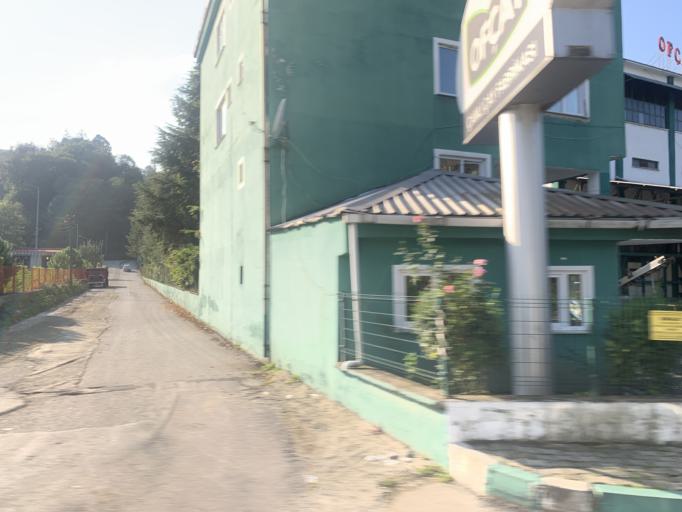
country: TR
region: Trabzon
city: Of
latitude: 40.9259
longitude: 40.2773
